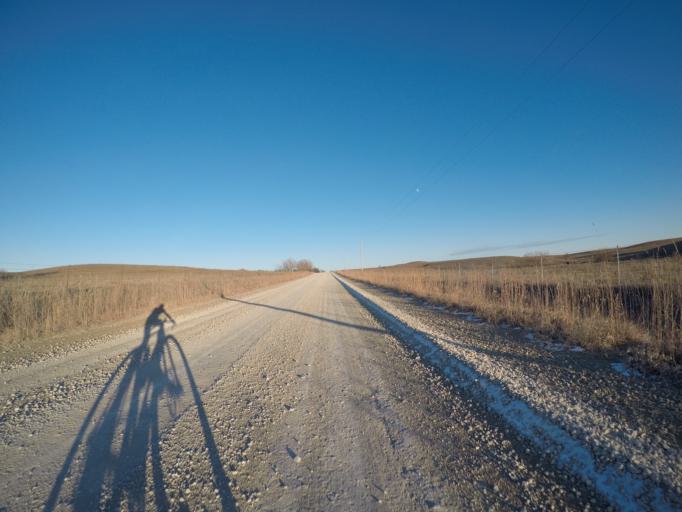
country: US
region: Kansas
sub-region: Pottawatomie County
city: Westmoreland
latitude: 39.3199
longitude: -96.5330
